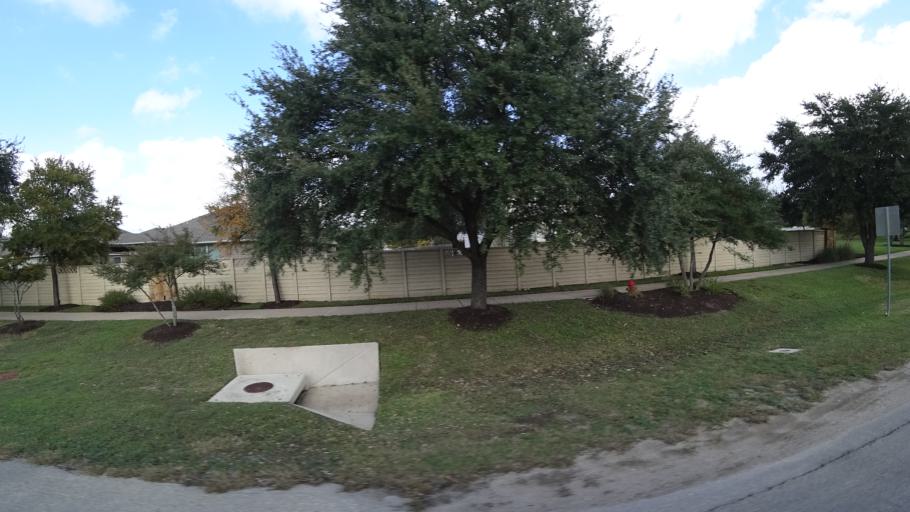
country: US
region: Texas
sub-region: Williamson County
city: Cedar Park
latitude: 30.4731
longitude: -97.8503
